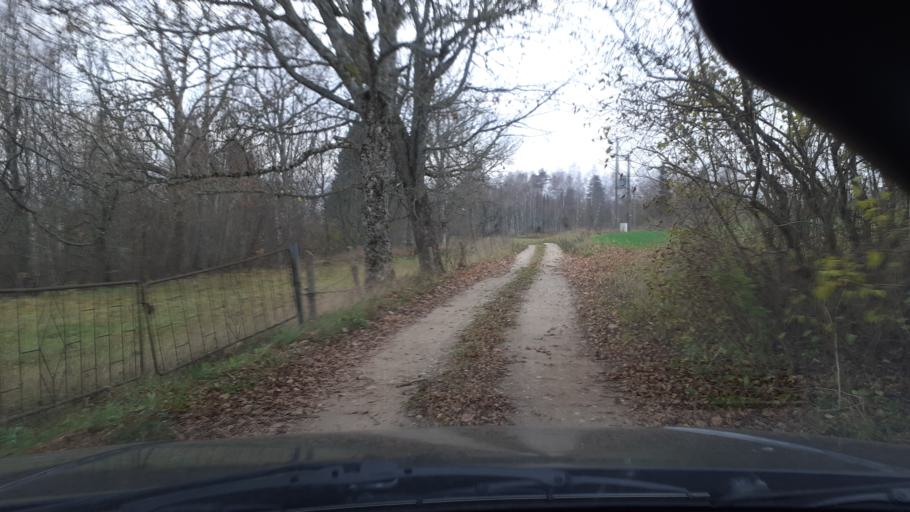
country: LV
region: Alsunga
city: Alsunga
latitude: 56.9440
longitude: 21.6417
